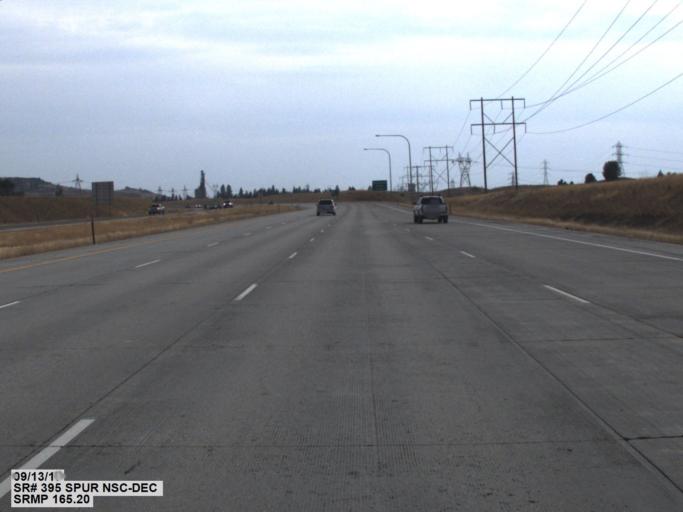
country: US
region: Washington
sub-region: Spokane County
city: Mead
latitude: 47.7658
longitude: -117.3672
